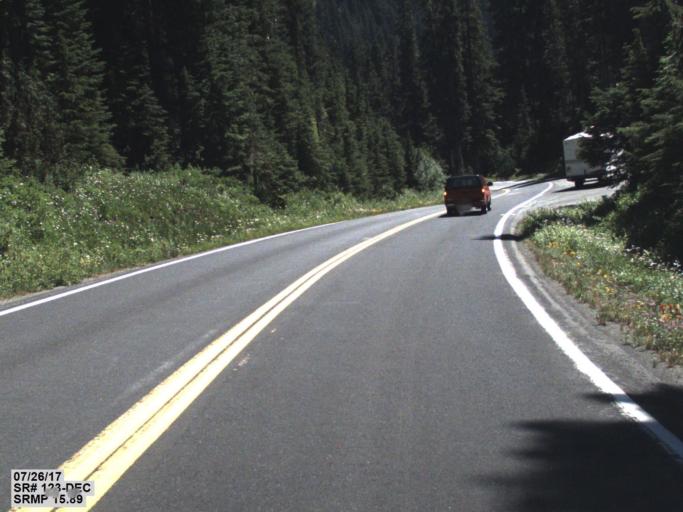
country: US
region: Washington
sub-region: King County
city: Enumclaw
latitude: 46.8653
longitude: -121.5332
